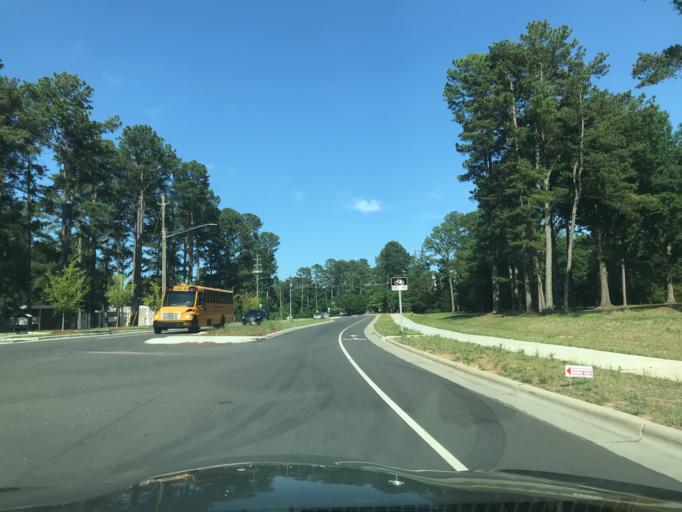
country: US
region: North Carolina
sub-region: Wake County
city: West Raleigh
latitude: 35.8704
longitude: -78.6272
